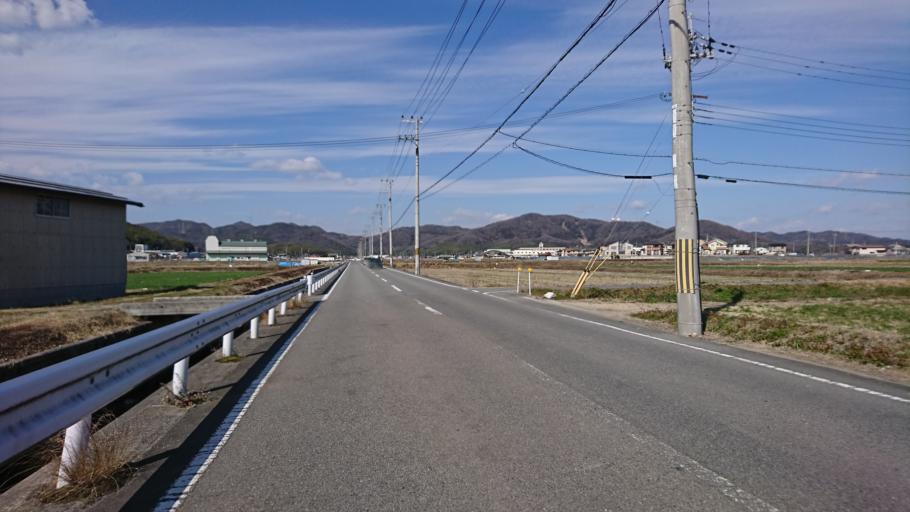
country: JP
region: Hyogo
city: Kakogawacho-honmachi
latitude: 34.8092
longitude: 134.8090
